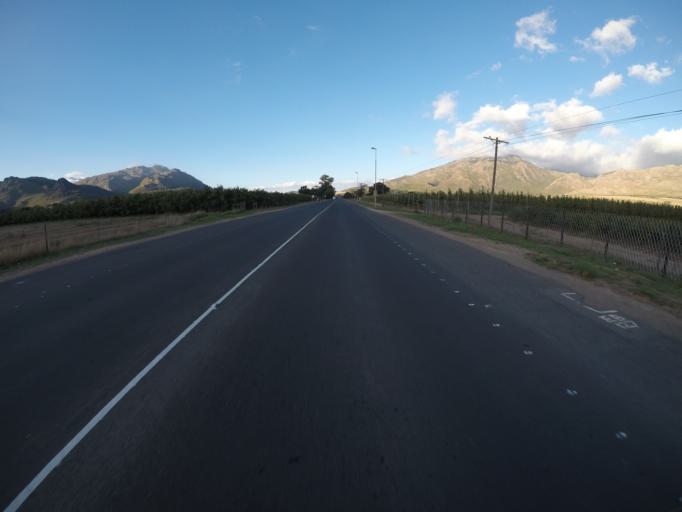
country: ZA
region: Western Cape
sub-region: Overberg District Municipality
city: Caledon
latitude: -33.9841
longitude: 19.2990
